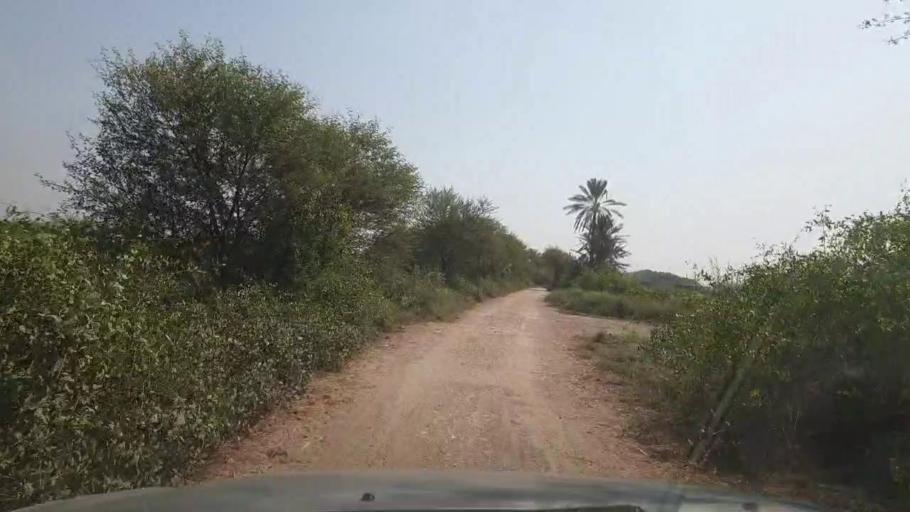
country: PK
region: Sindh
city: Bulri
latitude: 24.8832
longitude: 68.4021
